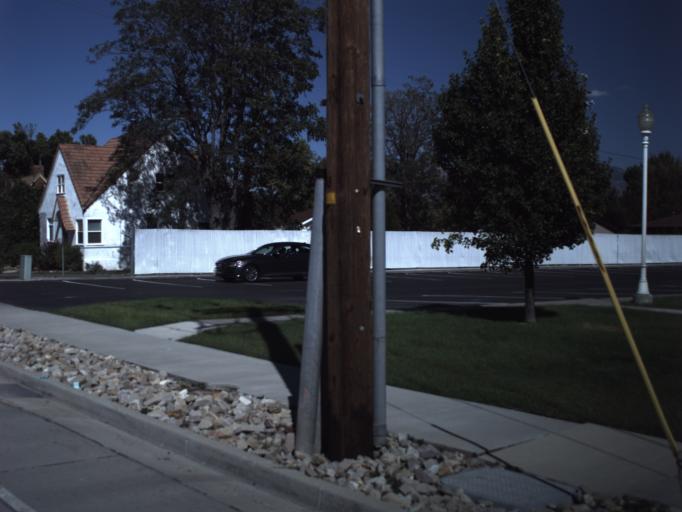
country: US
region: Utah
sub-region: Salt Lake County
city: Riverton
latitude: 40.5232
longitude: -111.9387
